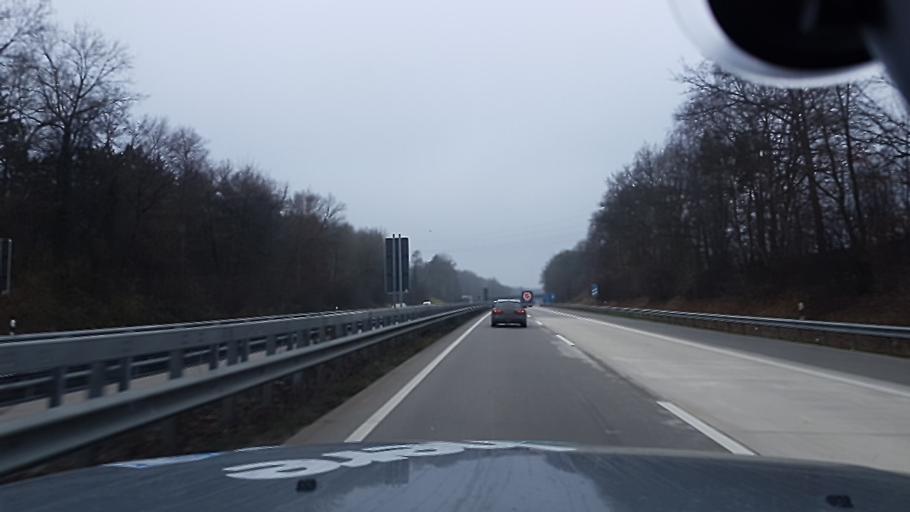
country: DE
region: Lower Saxony
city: Wildeshausen
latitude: 52.9163
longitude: 8.4596
